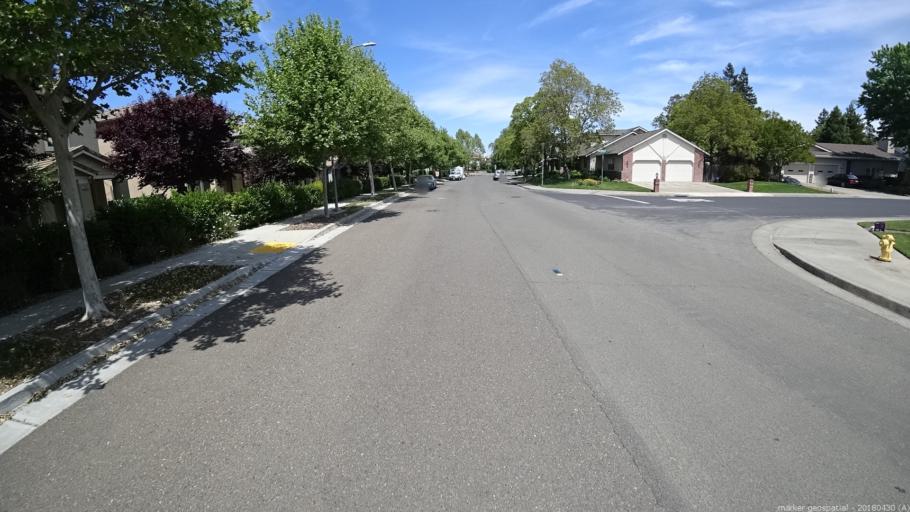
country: US
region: California
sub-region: Yolo County
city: West Sacramento
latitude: 38.5456
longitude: -121.5324
